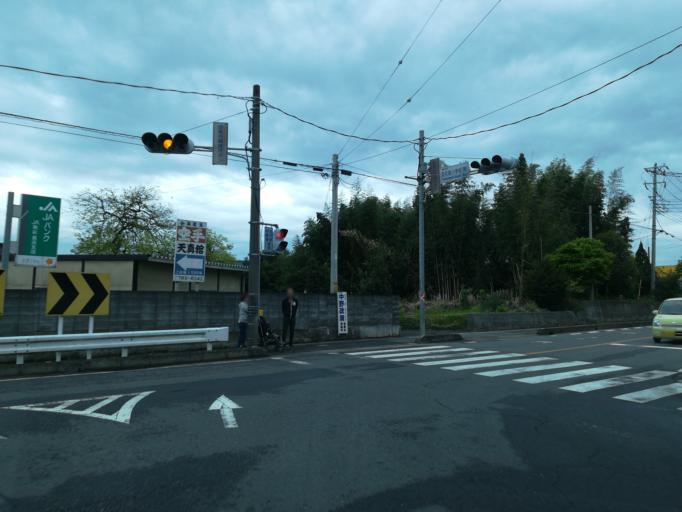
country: JP
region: Saitama
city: Hasuda
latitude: 35.9828
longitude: 139.6704
